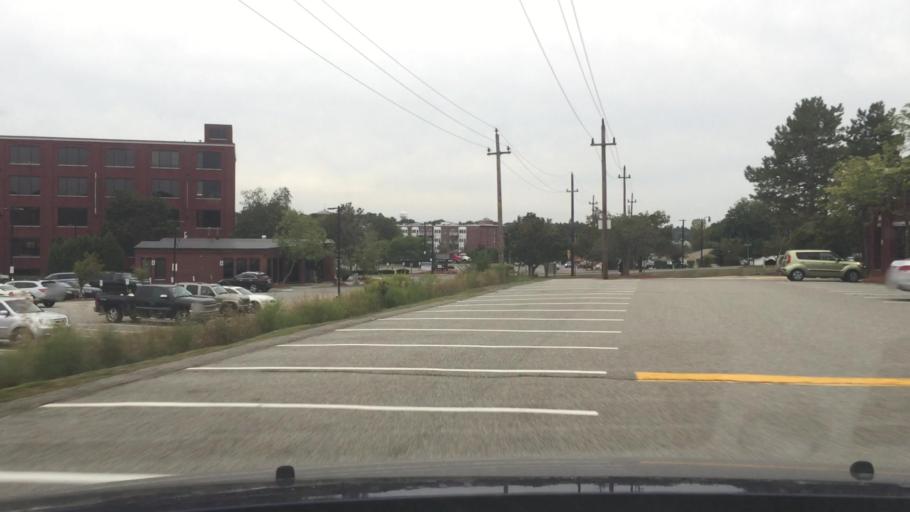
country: US
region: Massachusetts
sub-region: Essex County
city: North Andover
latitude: 42.7024
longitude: -71.1235
